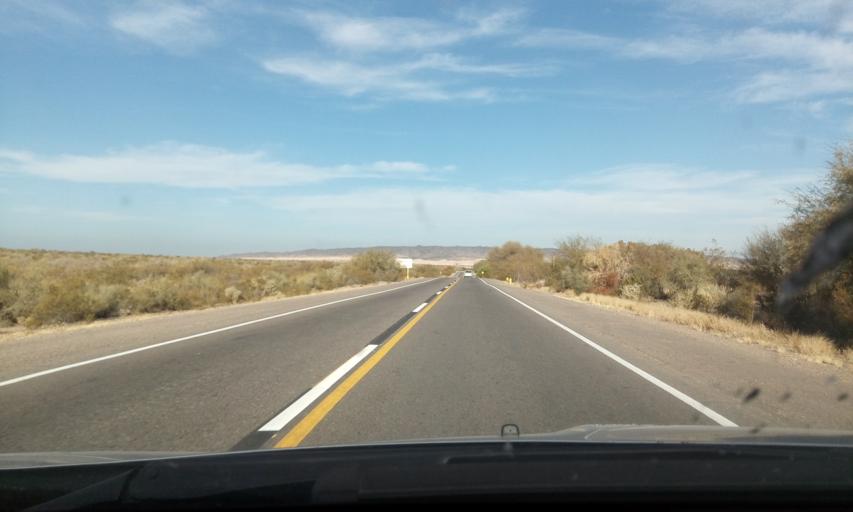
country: AR
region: San Juan
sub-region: Departamento de Rivadavia
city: Rivadavia
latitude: -31.4344
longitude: -68.6606
